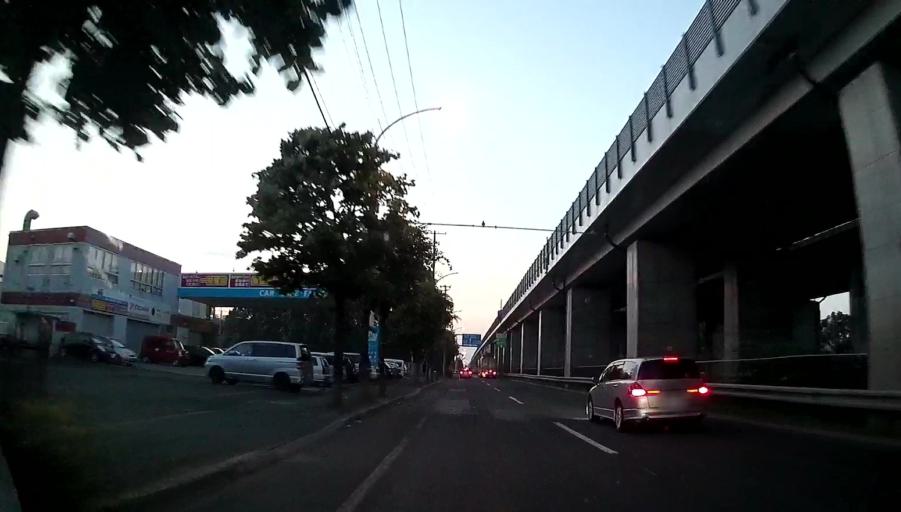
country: JP
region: Hokkaido
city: Sapporo
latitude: 43.0345
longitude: 141.4426
